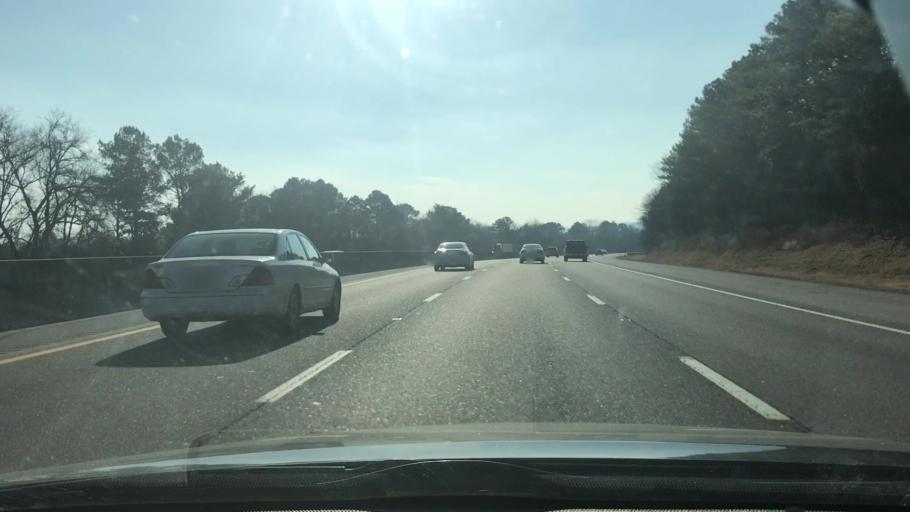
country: US
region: Tennessee
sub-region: Davidson County
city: Belle Meade
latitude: 36.0909
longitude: -86.9398
